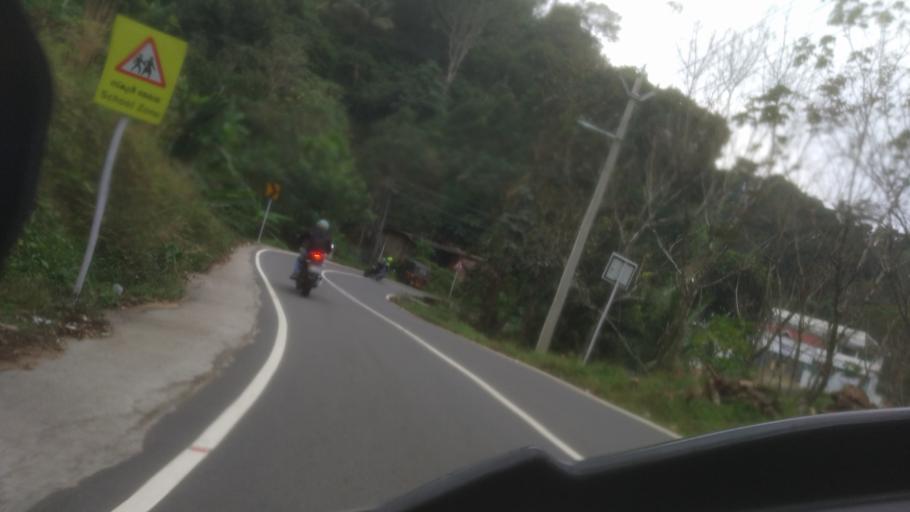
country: IN
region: Kerala
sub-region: Idukki
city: Idukki
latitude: 9.9526
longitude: 77.0119
